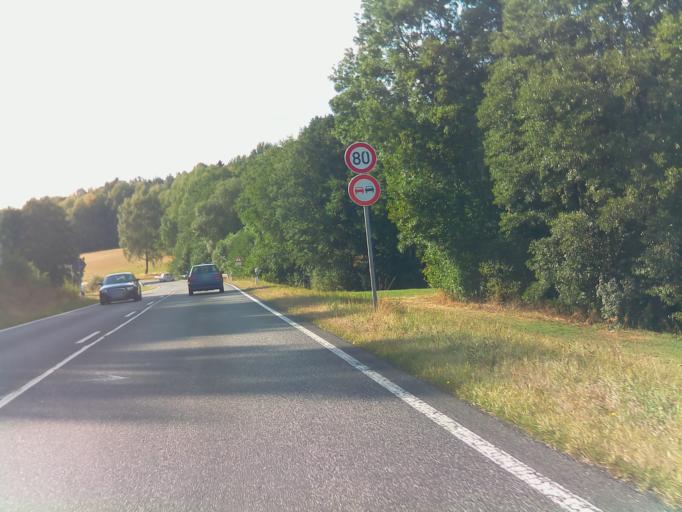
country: DE
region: Hesse
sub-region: Regierungsbezirk Kassel
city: Poppenhausen
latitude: 50.5127
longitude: 9.8646
